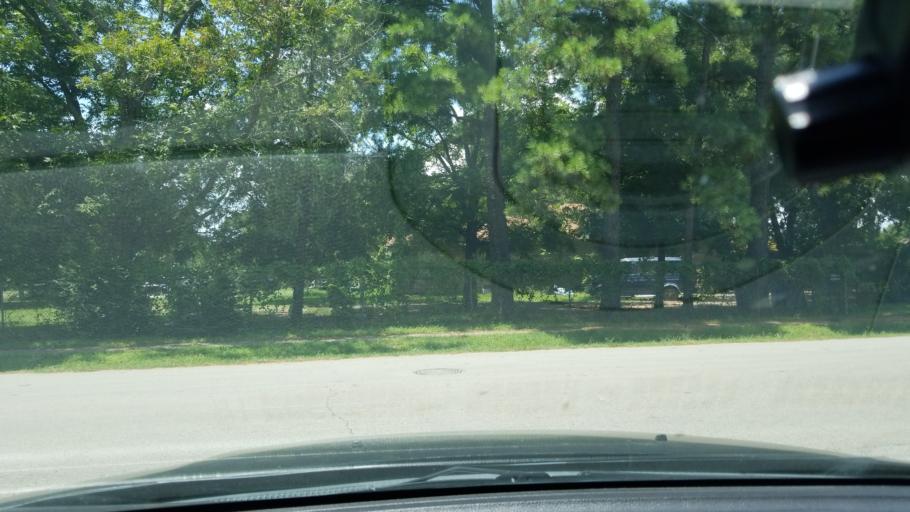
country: US
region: Texas
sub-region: Dallas County
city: Balch Springs
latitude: 32.7434
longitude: -96.6397
